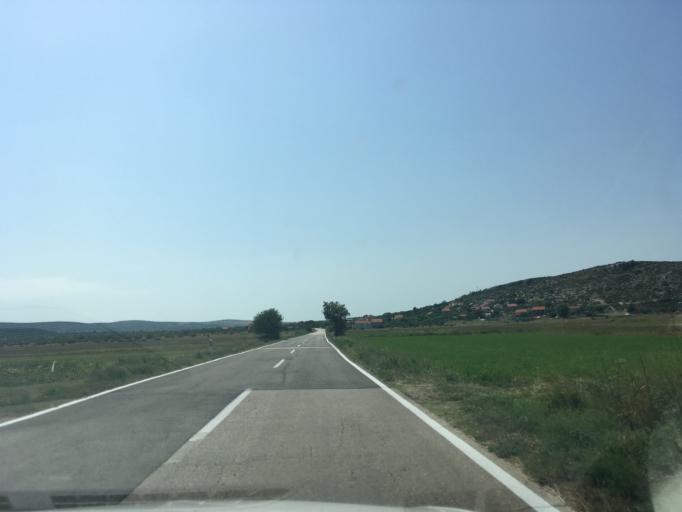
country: HR
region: Zadarska
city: Benkovac
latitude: 43.9630
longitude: 15.7598
